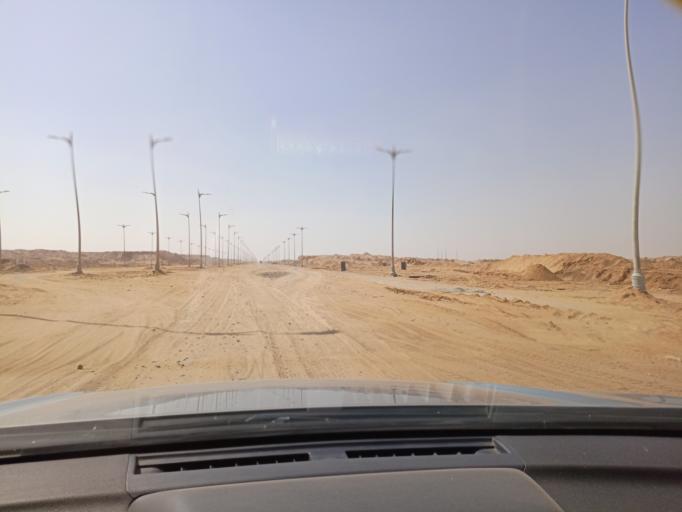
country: EG
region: Muhafazat al Qalyubiyah
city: Al Khankah
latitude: 30.0079
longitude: 31.6288
